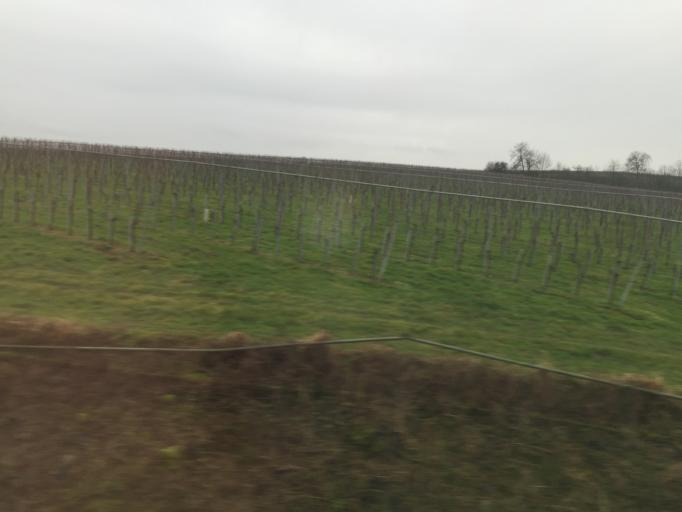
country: DE
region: Baden-Wuerttemberg
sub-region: Regierungsbezirk Stuttgart
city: Lauffen am Neckar
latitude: 49.0931
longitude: 9.1587
